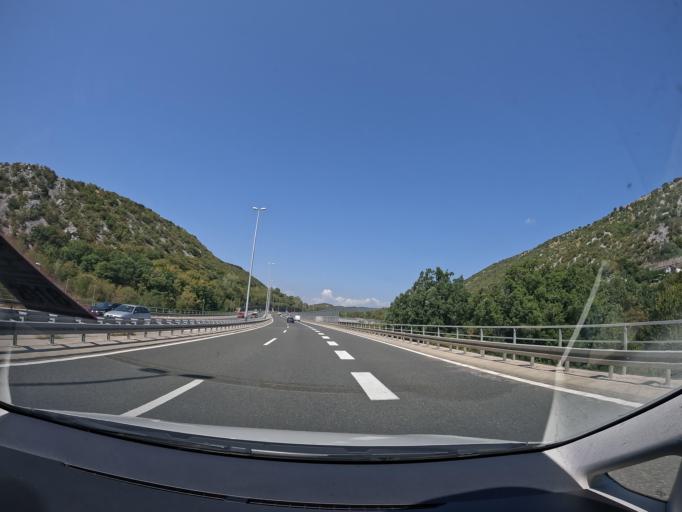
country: HR
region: Primorsko-Goranska
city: Skrljevo
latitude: 45.3035
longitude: 14.4952
